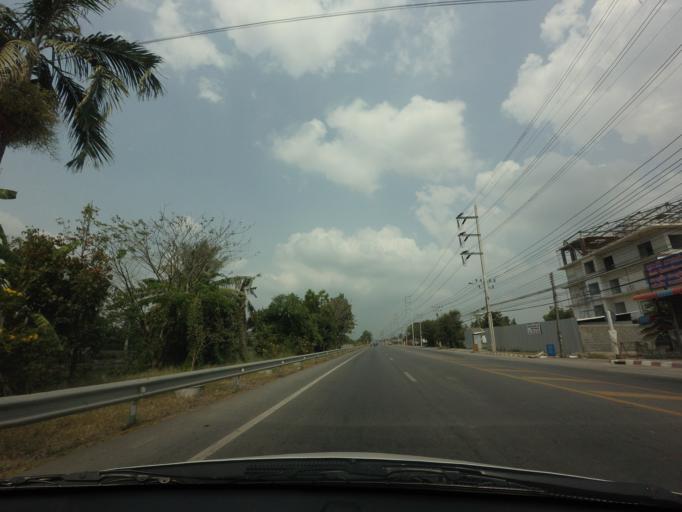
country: TH
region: Pathum Thani
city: Thanyaburi
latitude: 14.0605
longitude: 100.7102
